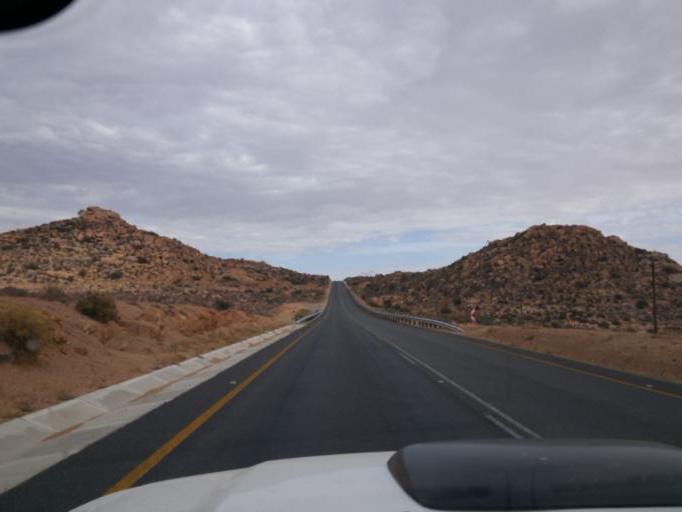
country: ZA
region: Northern Cape
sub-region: Namakwa District Municipality
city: Springbok
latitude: -29.4276
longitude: 17.8239
